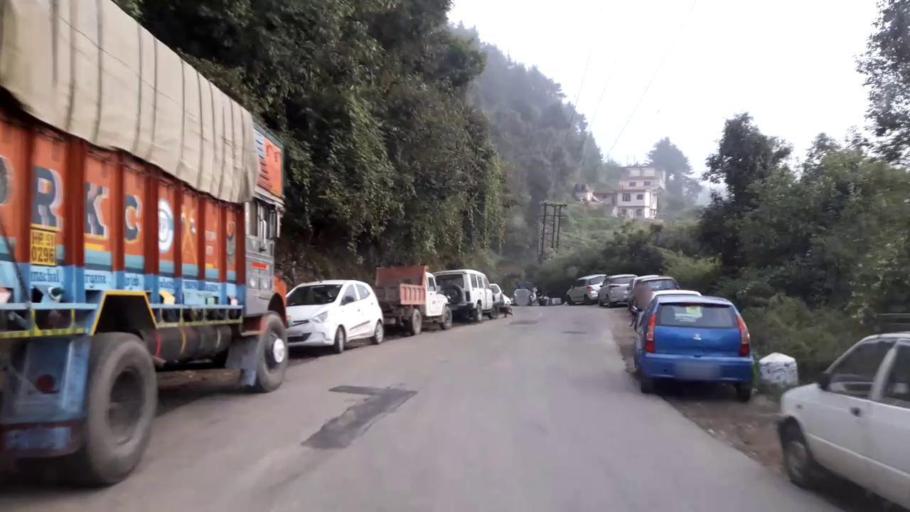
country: IN
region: Himachal Pradesh
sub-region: Shimla
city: Jutogh
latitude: 31.0429
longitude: 77.1277
